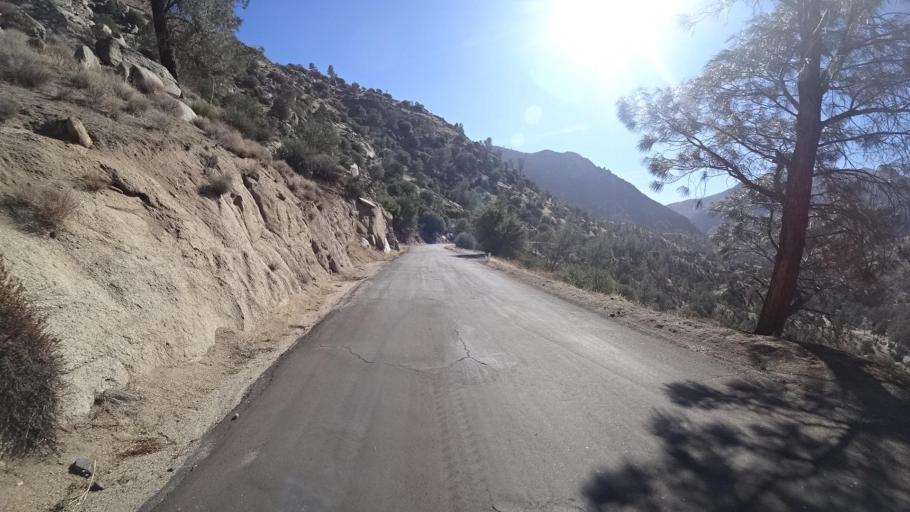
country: US
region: California
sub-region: Kern County
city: Bodfish
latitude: 35.5863
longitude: -118.5219
